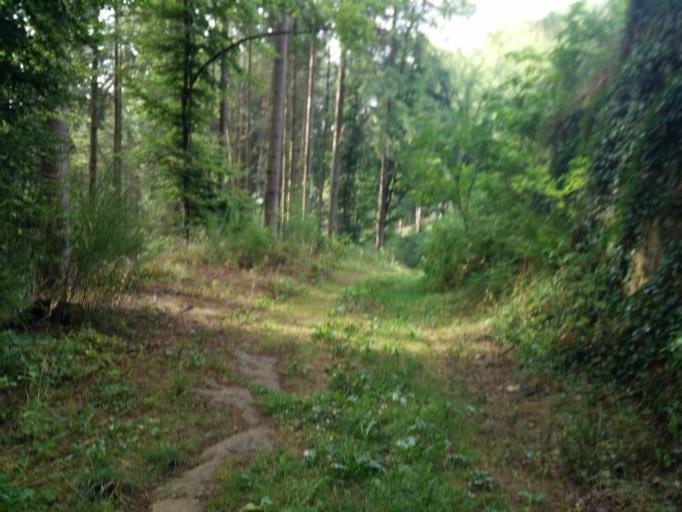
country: LU
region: Luxembourg
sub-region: Canton de Capellen
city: Mamer
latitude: 49.6393
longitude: 6.0460
